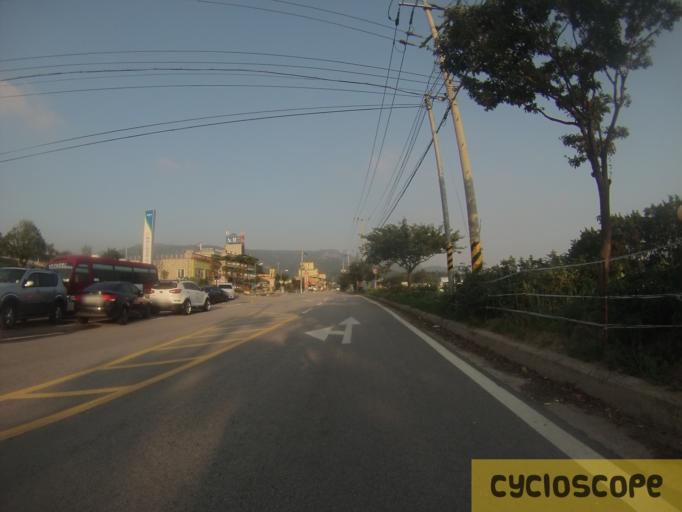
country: KR
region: Jeollabuk-do
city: Puan
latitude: 35.6367
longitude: 126.4646
